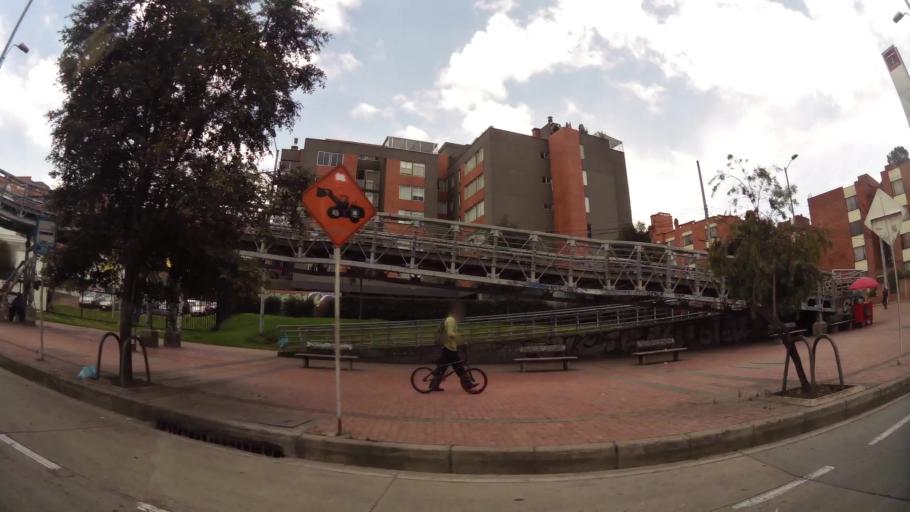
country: CO
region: Cundinamarca
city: Cota
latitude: 4.7350
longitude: -74.0801
